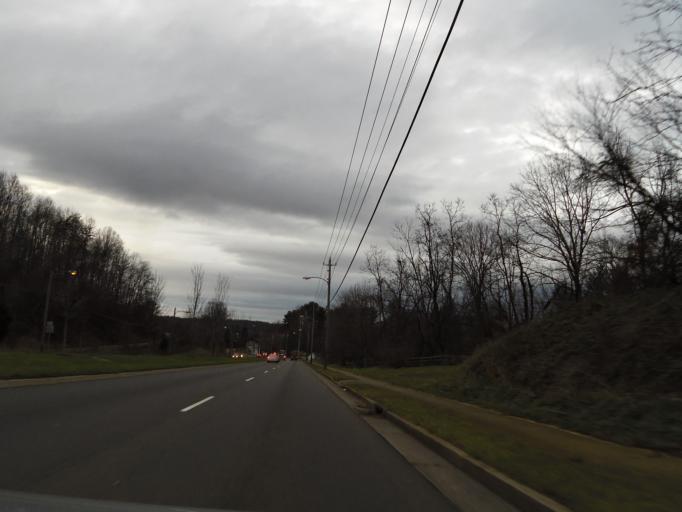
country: US
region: Tennessee
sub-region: Washington County
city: Johnson City
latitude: 36.3013
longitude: -82.3547
